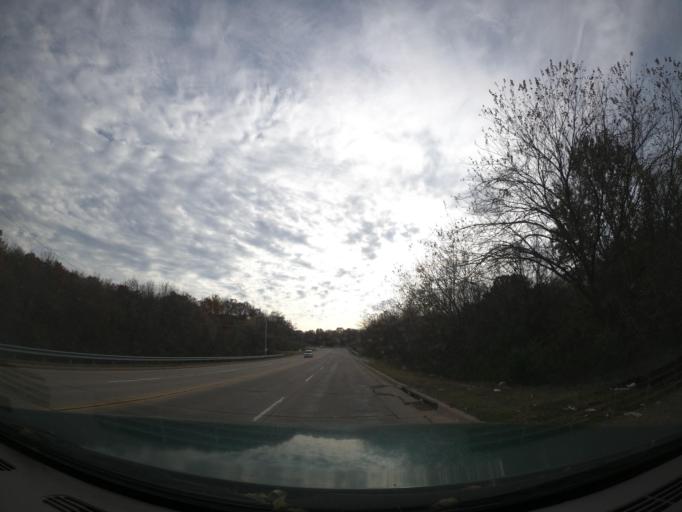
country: US
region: Oklahoma
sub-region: Tulsa County
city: Turley
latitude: 36.2151
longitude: -95.9954
